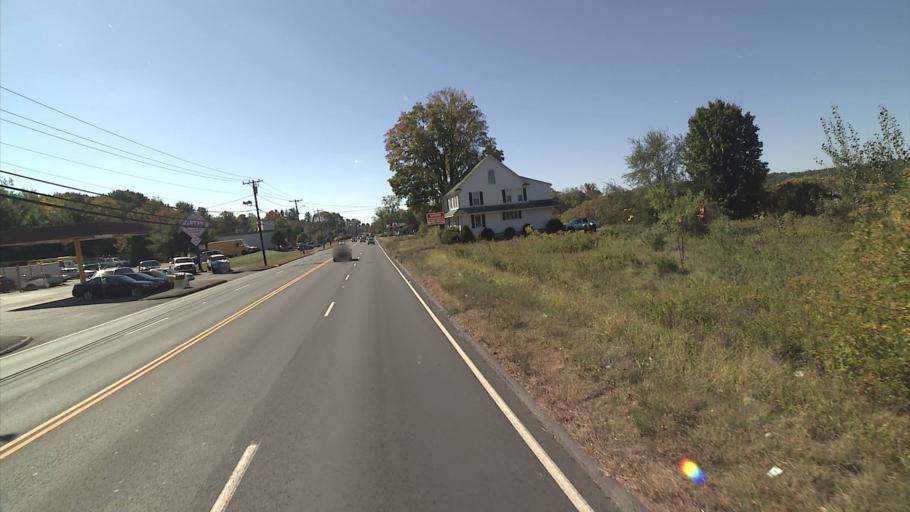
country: US
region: Connecticut
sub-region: Tolland County
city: Rockville
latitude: 41.8376
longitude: -72.4912
